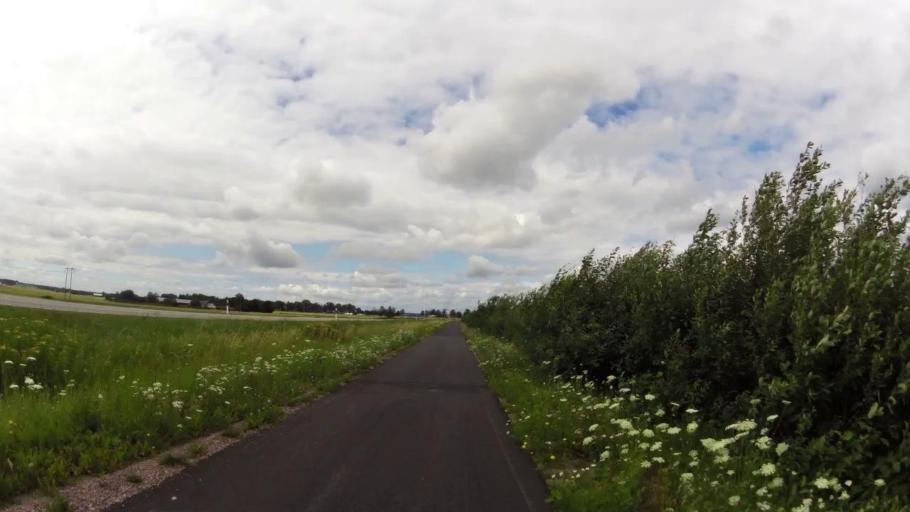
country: SE
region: OEstergoetland
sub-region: Linkopings Kommun
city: Linkoping
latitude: 58.4431
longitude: 15.5735
